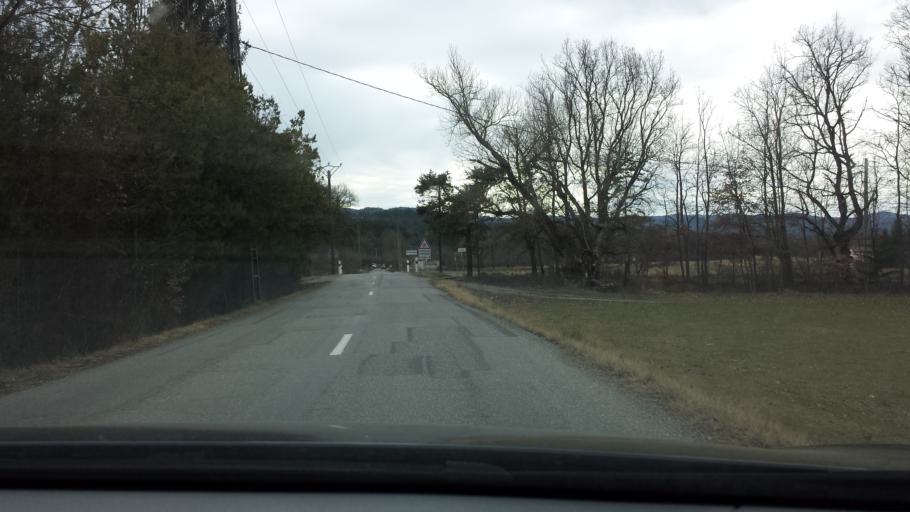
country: FR
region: Provence-Alpes-Cote d'Azur
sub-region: Departement des Alpes-de-Haute-Provence
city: Mallemoisson
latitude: 44.0612
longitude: 6.1780
